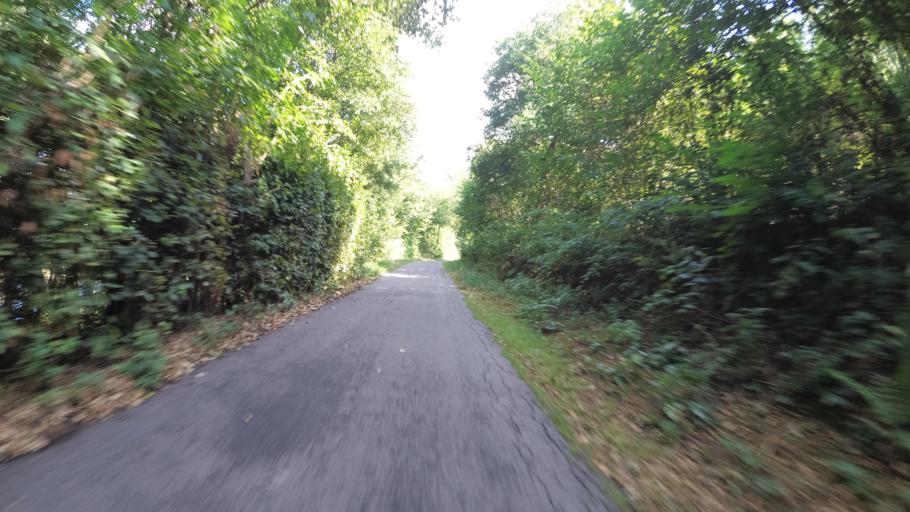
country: DE
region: Saarland
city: Mainzweiler
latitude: 49.4036
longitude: 7.0947
